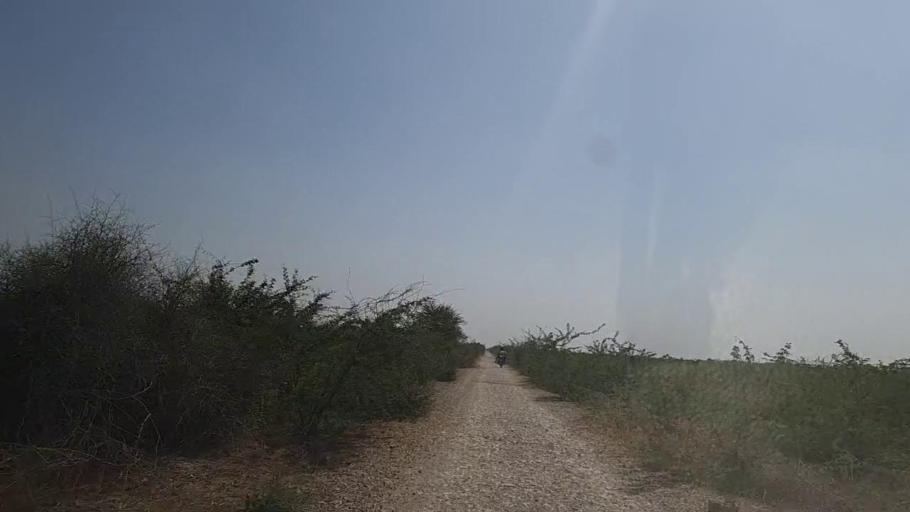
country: PK
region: Sindh
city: Naukot
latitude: 24.6456
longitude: 69.2755
